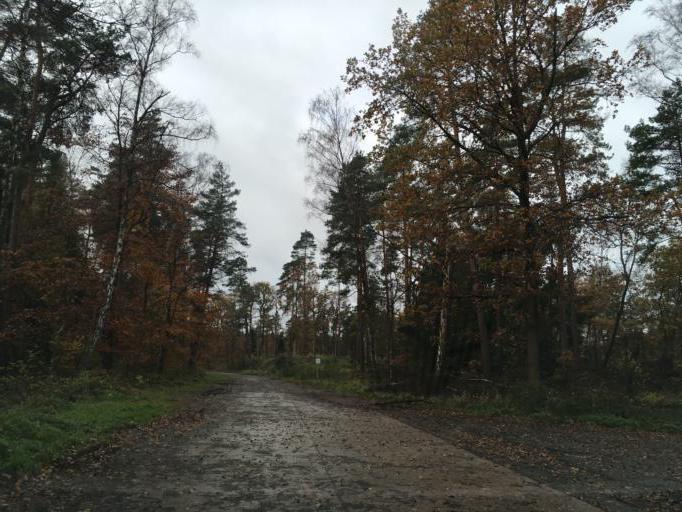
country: DE
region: Lower Saxony
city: Barendorf
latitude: 53.2505
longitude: 10.4970
